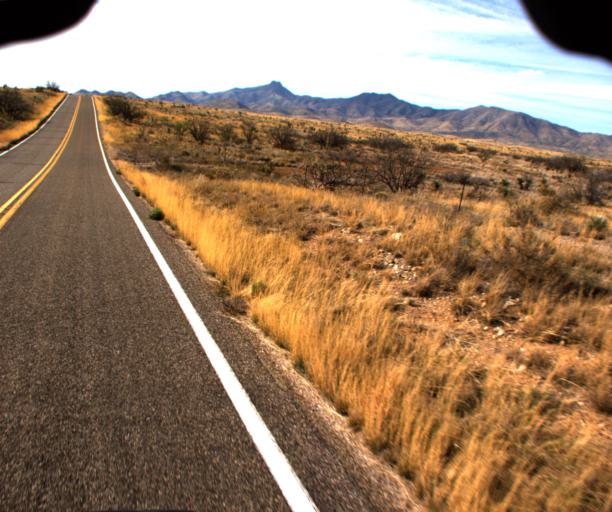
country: US
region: Arizona
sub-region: Cochise County
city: Willcox
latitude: 32.0994
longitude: -109.5406
